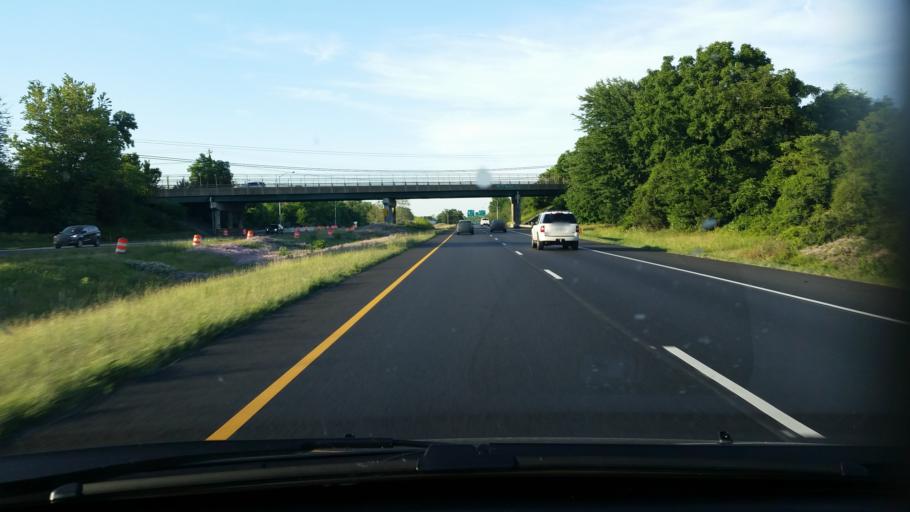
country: US
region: Maryland
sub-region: Washington County
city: Halfway
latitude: 39.6479
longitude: -77.7550
